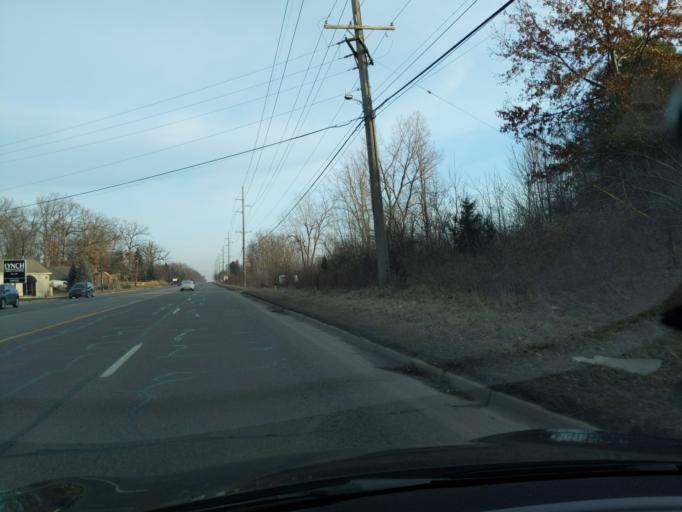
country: US
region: Michigan
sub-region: Livingston County
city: Howell
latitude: 42.5785
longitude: -83.8503
